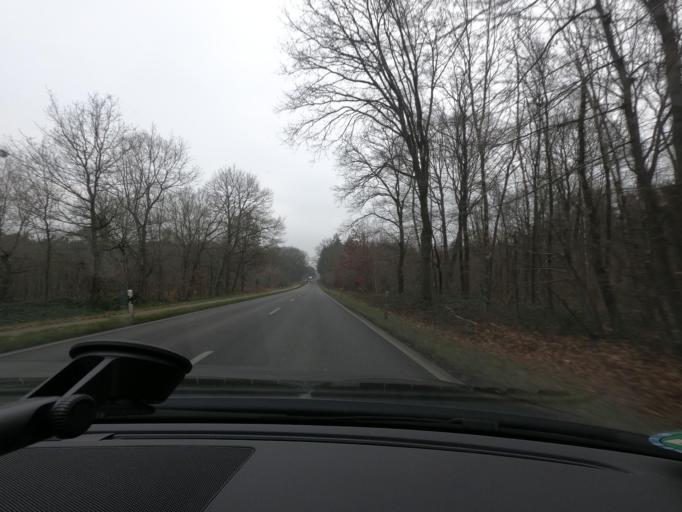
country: DE
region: North Rhine-Westphalia
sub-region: Regierungsbezirk Dusseldorf
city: Nettetal
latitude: 51.3511
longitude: 6.2354
